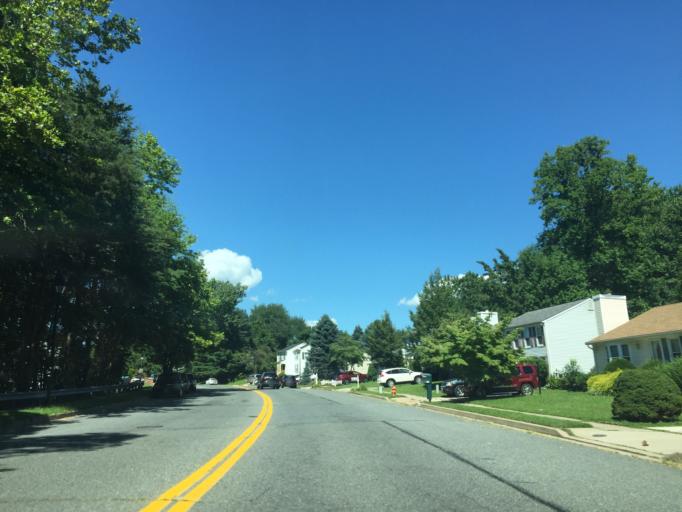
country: US
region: Maryland
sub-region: Baltimore County
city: Perry Hall
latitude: 39.4111
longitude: -76.4789
